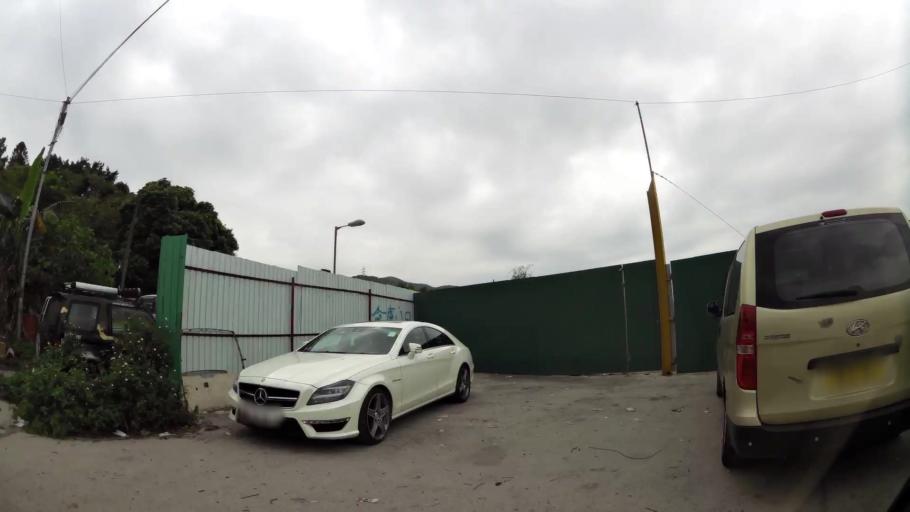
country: HK
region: Yuen Long
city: Yuen Long Kau Hui
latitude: 22.4414
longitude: 113.9900
